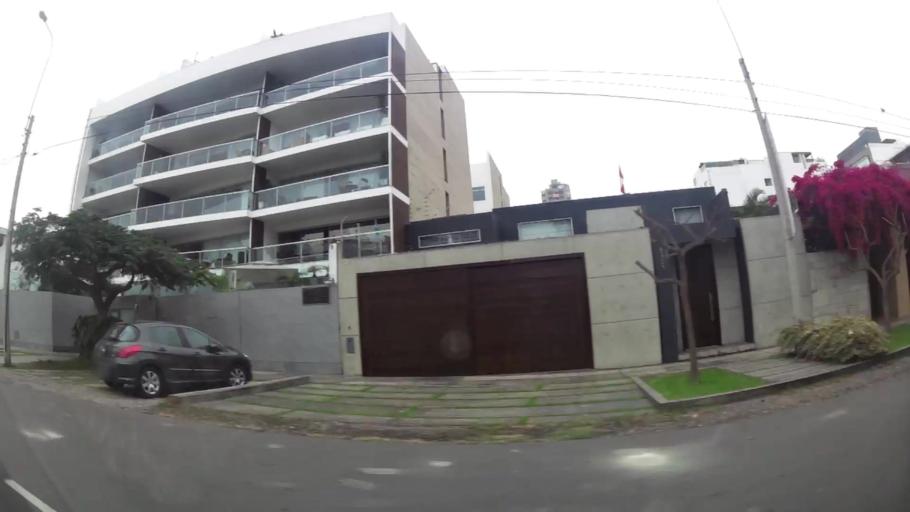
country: PE
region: Lima
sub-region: Lima
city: Surco
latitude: -12.1316
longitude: -77.0246
